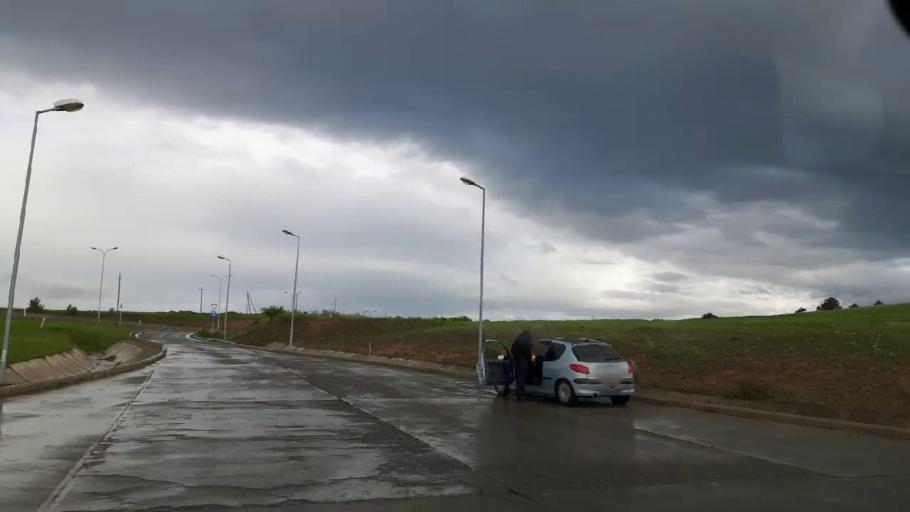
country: GE
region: Shida Kartli
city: Gori
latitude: 42.0144
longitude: 44.0324
